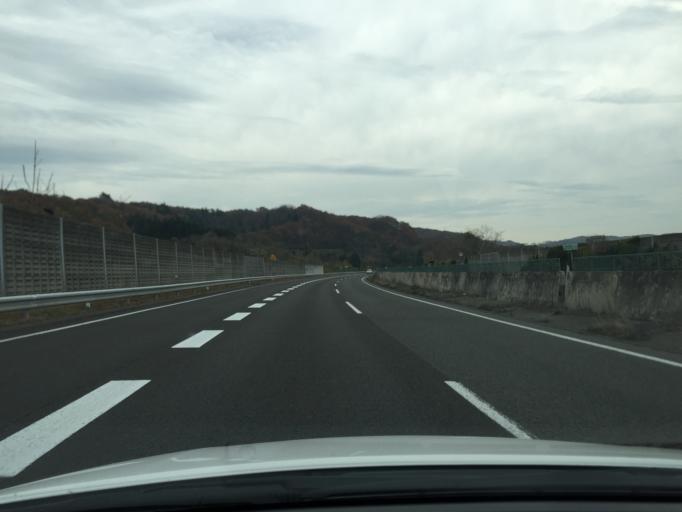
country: JP
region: Fukushima
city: Fukushima-shi
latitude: 37.7058
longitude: 140.4509
